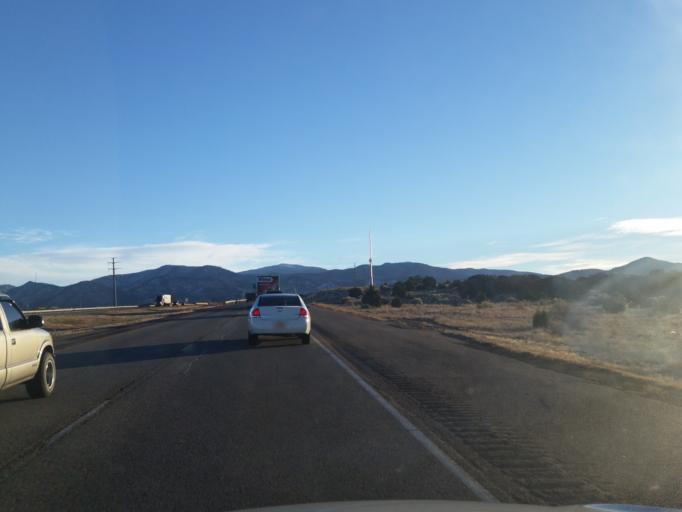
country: US
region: New Mexico
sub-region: Santa Fe County
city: Agua Fria
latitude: 35.6304
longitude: -105.9684
